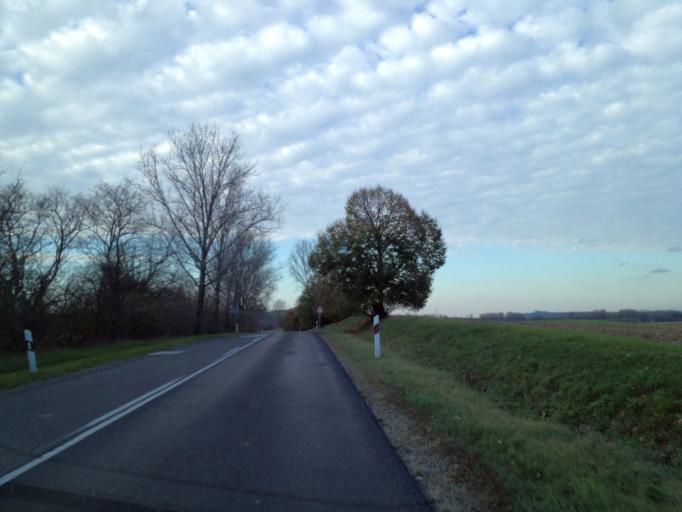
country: HU
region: Gyor-Moson-Sopron
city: Bakonyszentlaszlo
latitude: 47.4556
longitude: 17.8077
